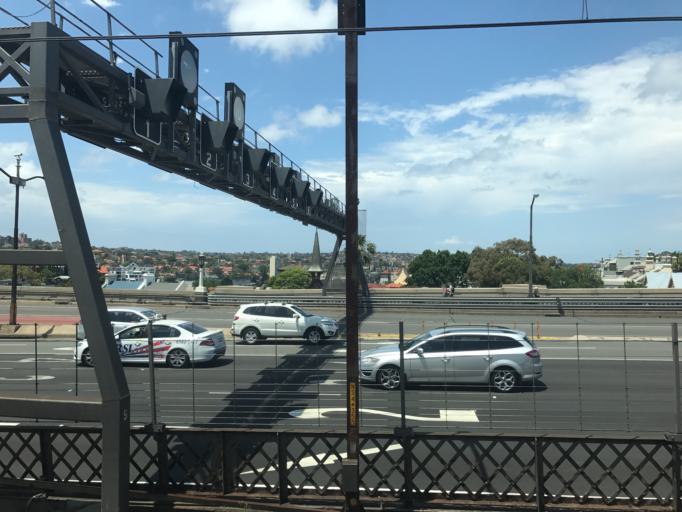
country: AU
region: New South Wales
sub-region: North Sydney
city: Milsons Point
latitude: -33.8469
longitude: 151.2123
